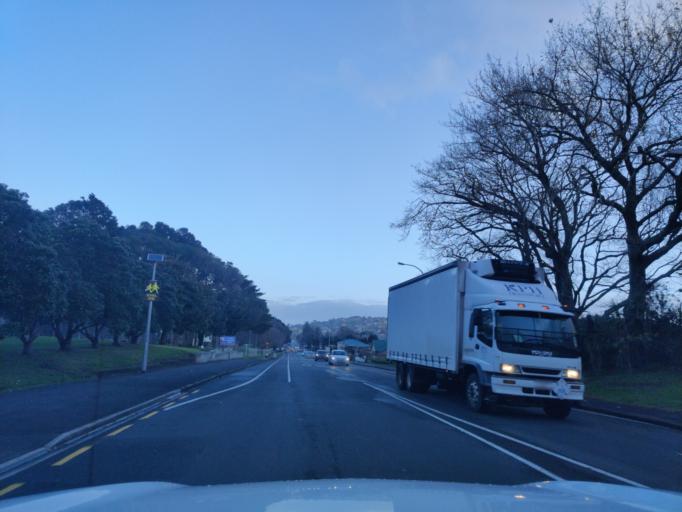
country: NZ
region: Auckland
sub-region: Auckland
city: Pukekohe East
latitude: -37.2020
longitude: 174.9011
